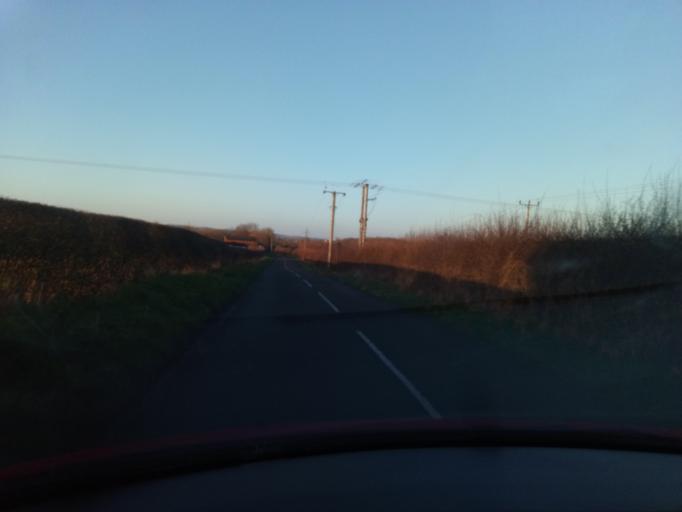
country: GB
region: England
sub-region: Leicestershire
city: Barrow upon Soar
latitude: 52.7723
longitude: -1.1573
